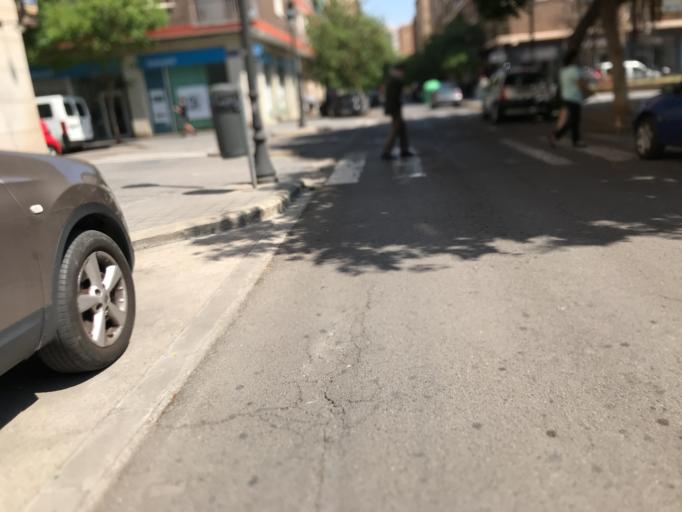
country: ES
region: Valencia
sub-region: Provincia de Valencia
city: Valencia
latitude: 39.4680
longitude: -0.3475
